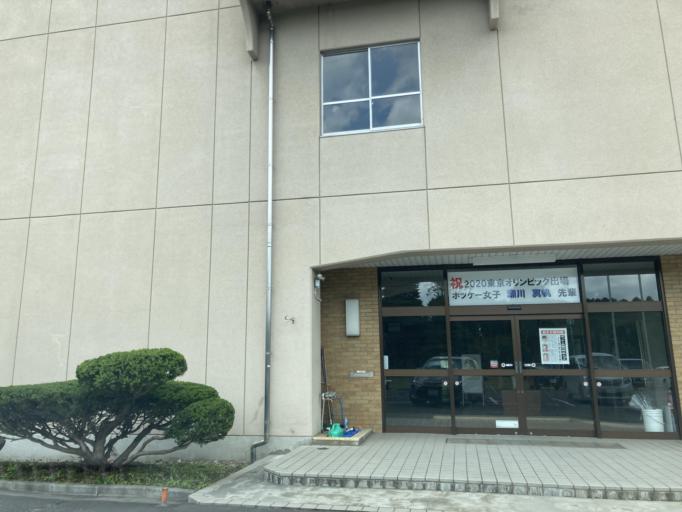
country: JP
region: Iwate
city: Ichinohe
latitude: 39.9690
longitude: 141.2118
